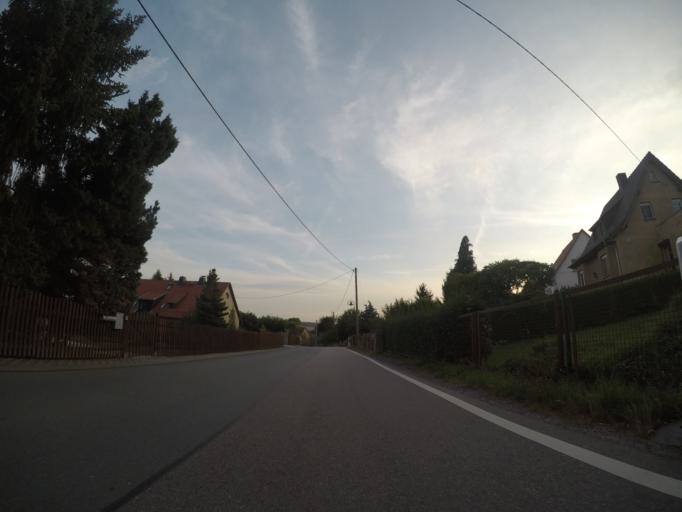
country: DE
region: Thuringia
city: Nobdenitz
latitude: 50.8903
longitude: 12.2945
